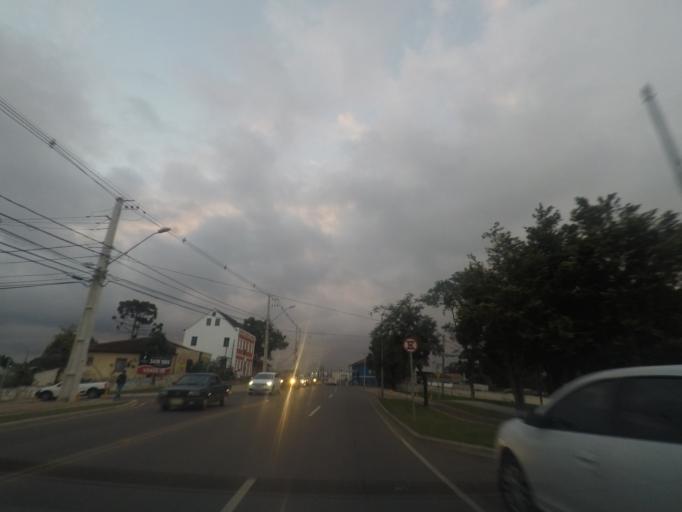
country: BR
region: Parana
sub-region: Almirante Tamandare
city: Almirante Tamandare
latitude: -25.3933
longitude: -49.3503
